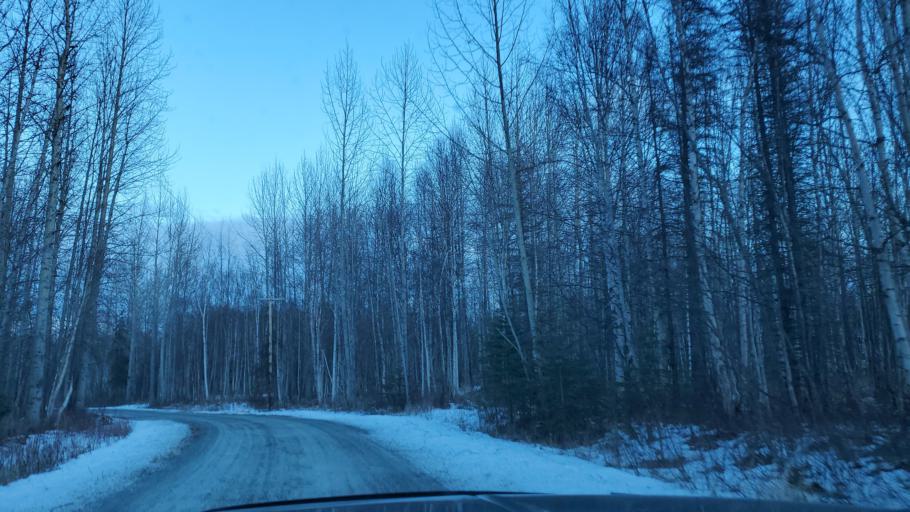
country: US
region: Alaska
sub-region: Matanuska-Susitna Borough
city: Lakes
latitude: 61.6658
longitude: -149.3342
